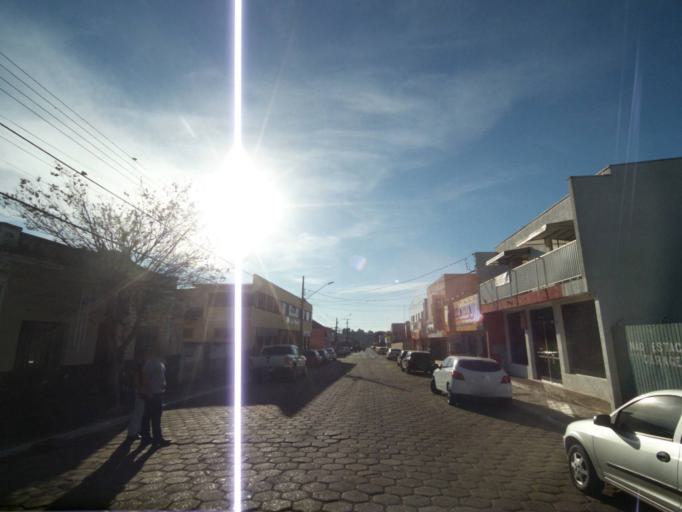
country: BR
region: Parana
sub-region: Tibagi
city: Tibagi
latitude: -24.5142
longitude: -50.4115
